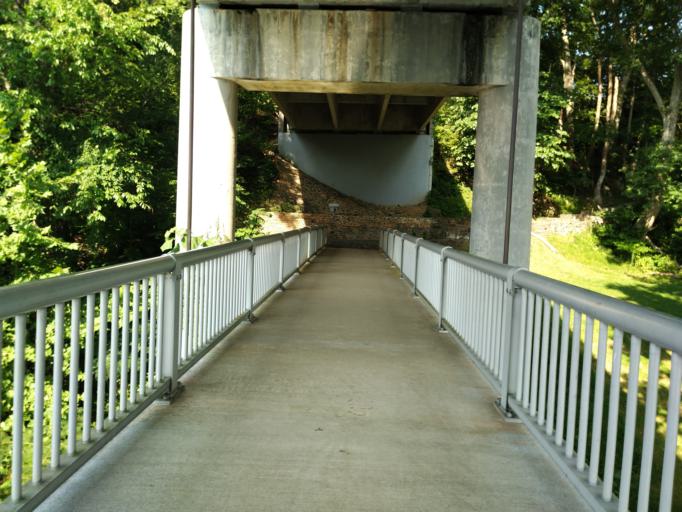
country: US
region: Virginia
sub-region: Rockbridge County
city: Glasgow
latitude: 37.5554
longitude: -79.3667
